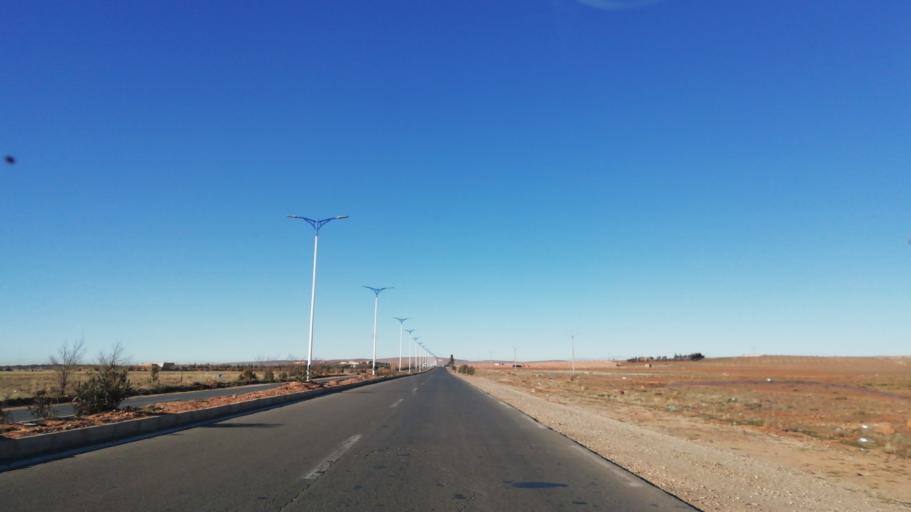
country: DZ
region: El Bayadh
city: El Bayadh
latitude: 33.6895
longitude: 1.0654
